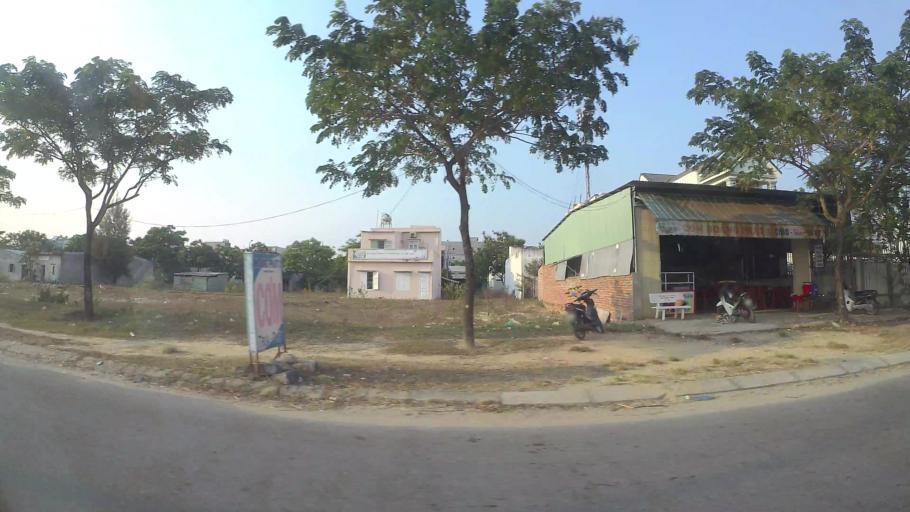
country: VN
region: Da Nang
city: Ngu Hanh Son
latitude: 15.9780
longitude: 108.2507
